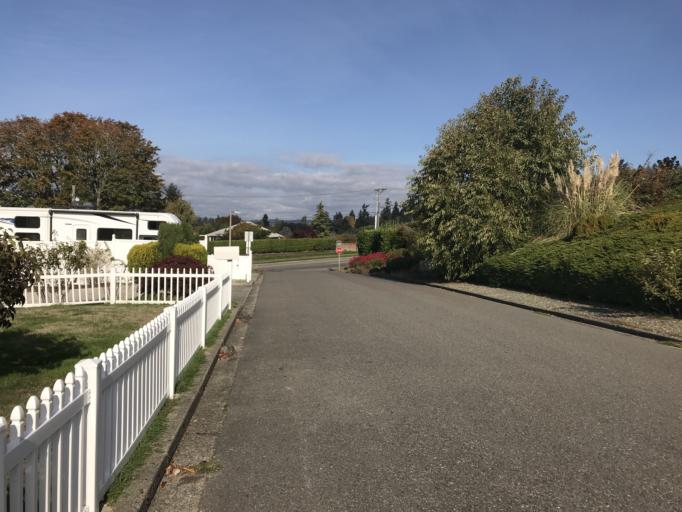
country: US
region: Washington
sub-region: Pierce County
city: University Place
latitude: 47.2521
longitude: -122.5423
